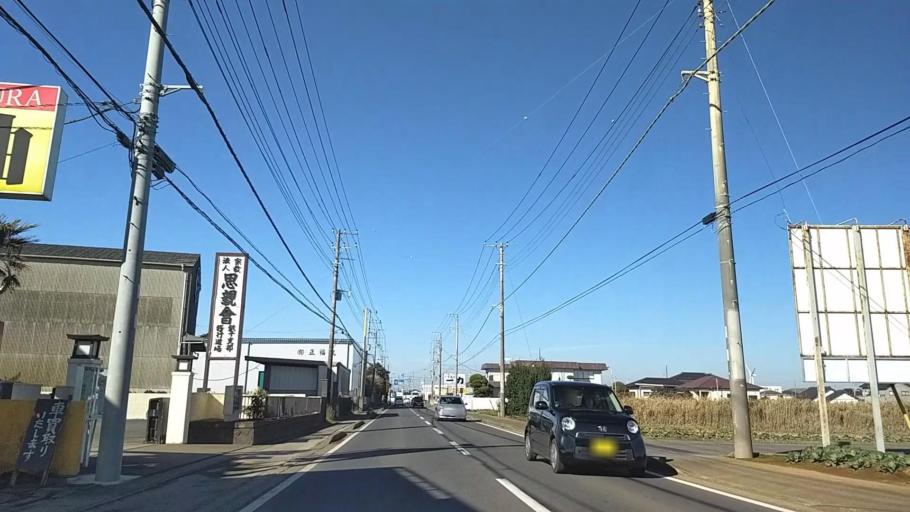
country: JP
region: Chiba
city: Hasaki
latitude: 35.7125
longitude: 140.7752
